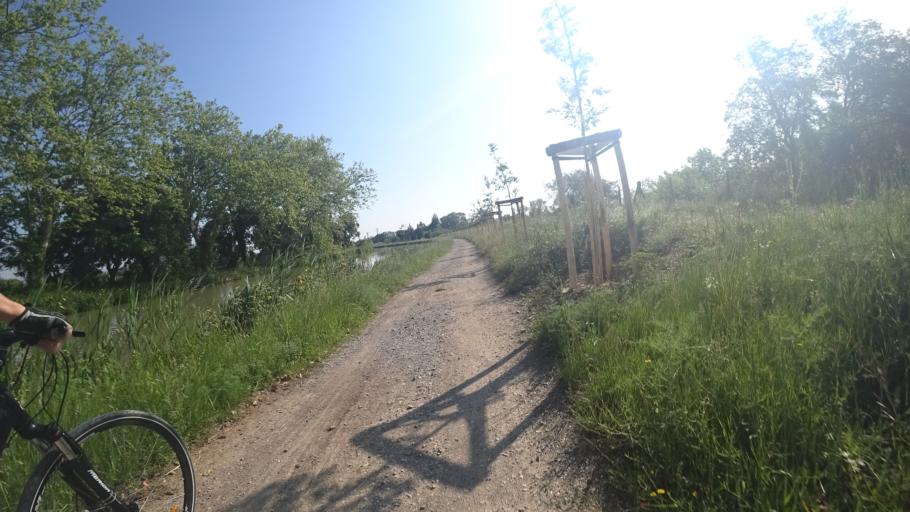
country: FR
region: Languedoc-Roussillon
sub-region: Departement de l'Aude
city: Saint-Marcel-sur-Aude
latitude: 43.2735
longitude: 2.9138
